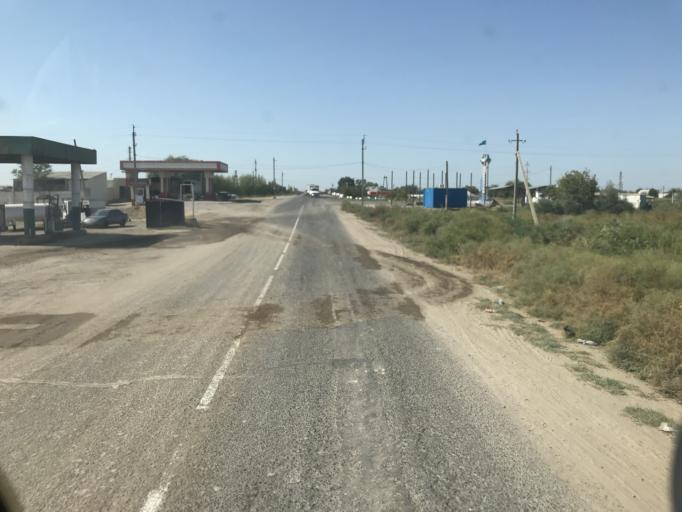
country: KZ
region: Ongtustik Qazaqstan
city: Myrzakent
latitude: 40.6704
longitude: 68.5520
